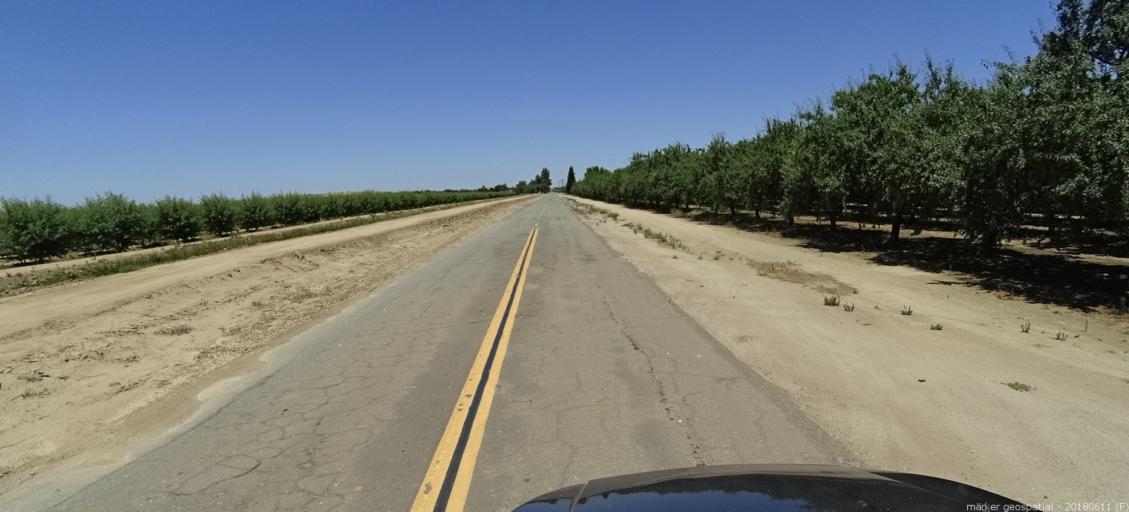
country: US
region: California
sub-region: Madera County
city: Fairmead
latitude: 37.0547
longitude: -120.1934
